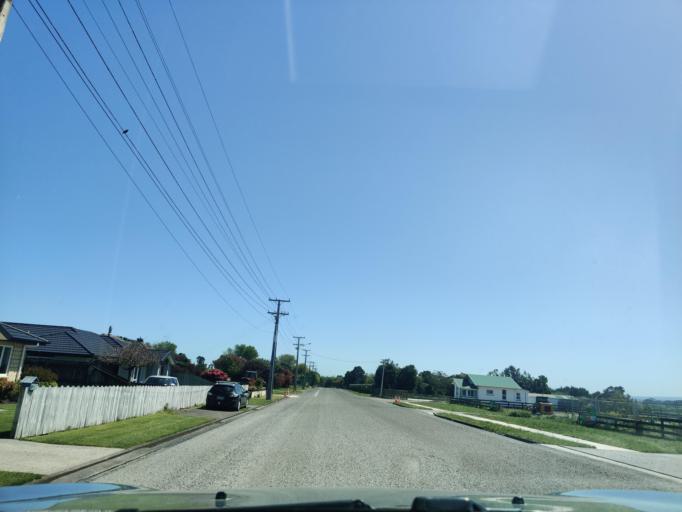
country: NZ
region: Taranaki
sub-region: South Taranaki District
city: Hawera
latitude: -39.5903
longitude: 174.2652
